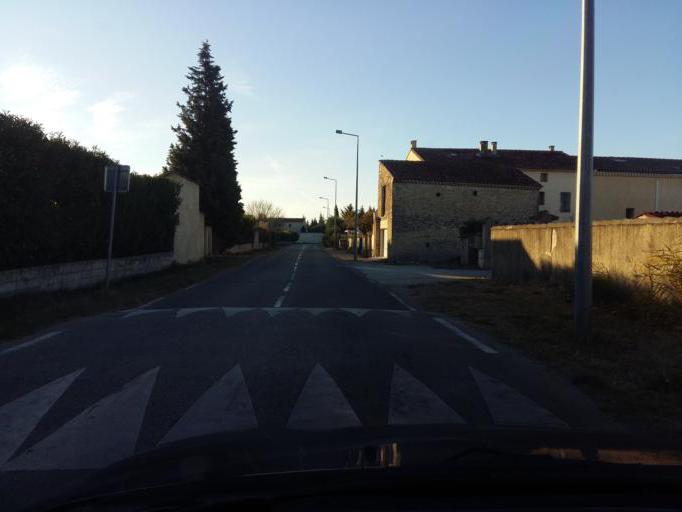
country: FR
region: Provence-Alpes-Cote d'Azur
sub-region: Departement du Vaucluse
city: Monteux
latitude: 44.0342
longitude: 4.9811
